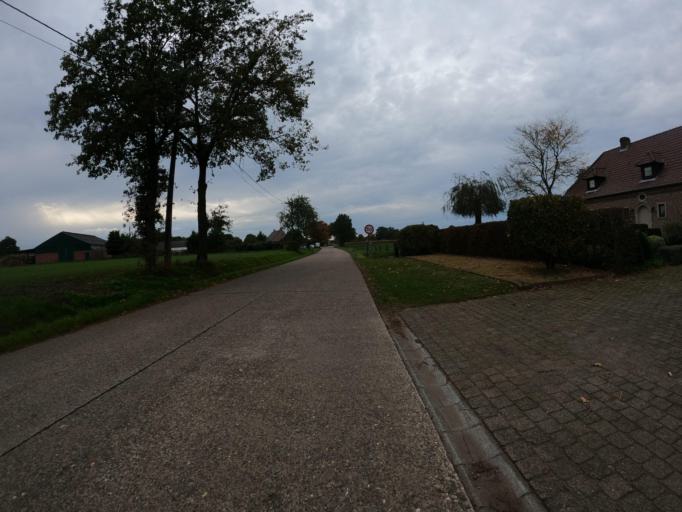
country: BE
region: Flanders
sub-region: Provincie Antwerpen
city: Herselt
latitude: 51.0920
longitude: 4.8542
